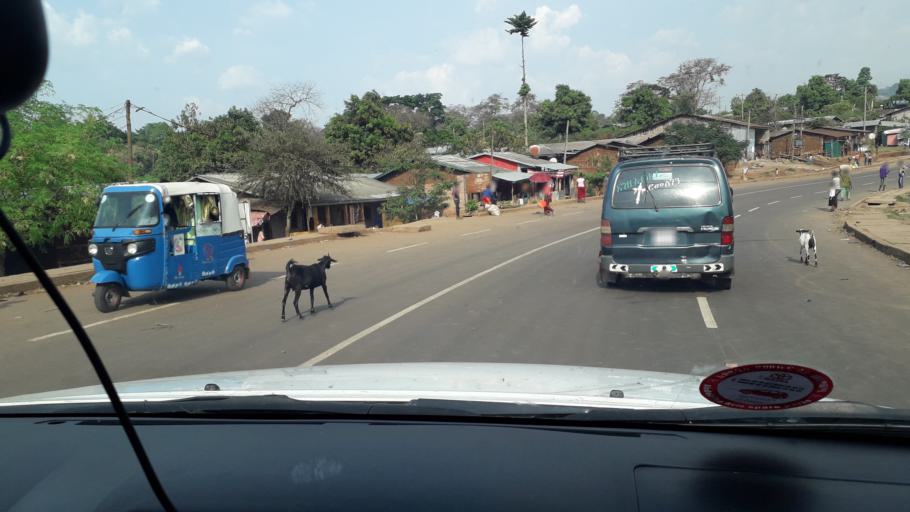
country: ET
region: Southern Nations, Nationalities, and People's Region
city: Mizan Teferi
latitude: 6.8561
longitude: 35.3303
